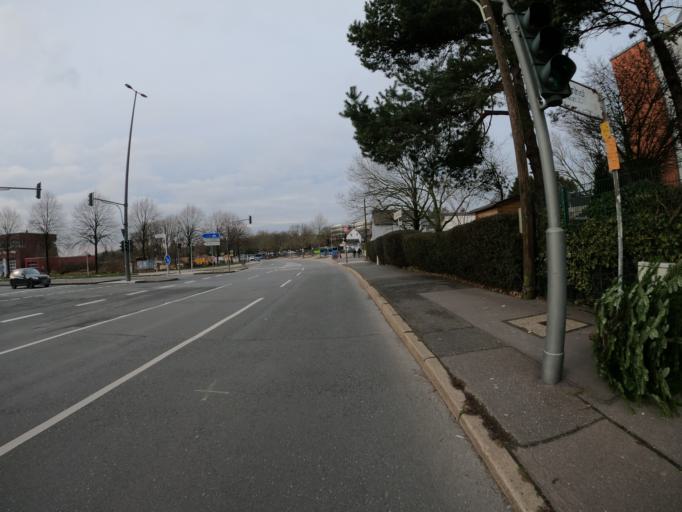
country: DE
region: North Rhine-Westphalia
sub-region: Regierungsbezirk Dusseldorf
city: Wuppertal
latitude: 51.2298
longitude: 7.1451
